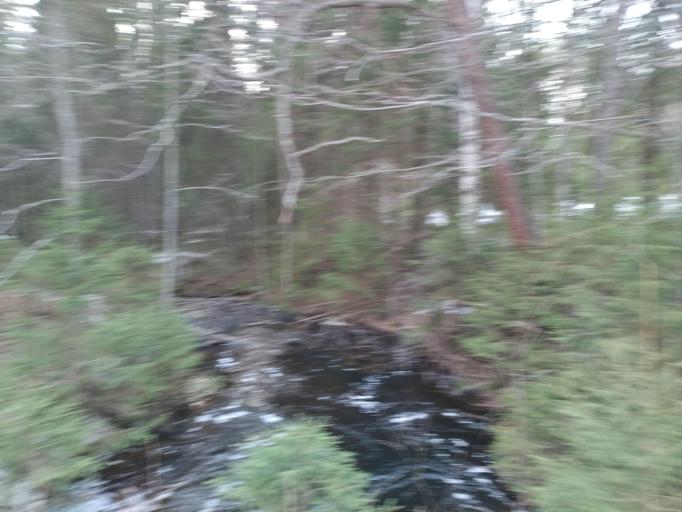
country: FI
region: South Karelia
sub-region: Lappeenranta
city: Savitaipale
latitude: 61.4887
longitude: 27.7901
